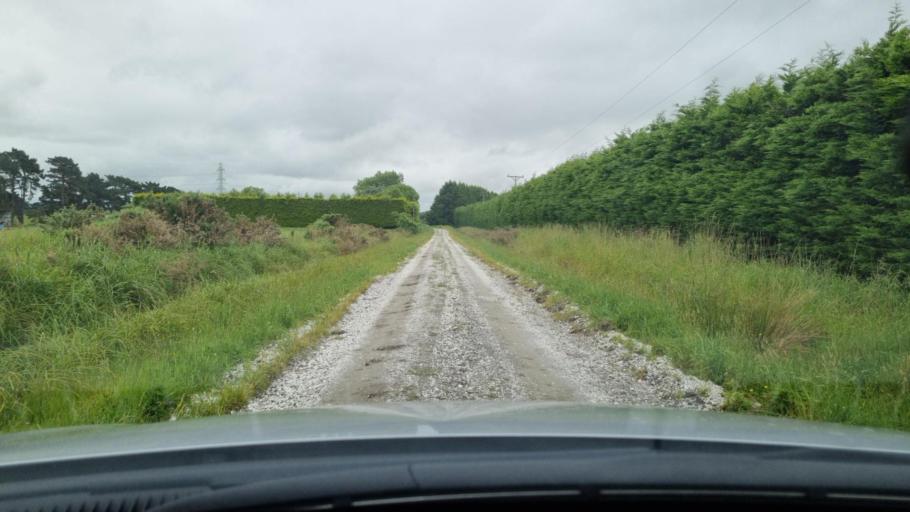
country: NZ
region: Southland
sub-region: Invercargill City
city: Invercargill
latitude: -46.3904
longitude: 168.4048
